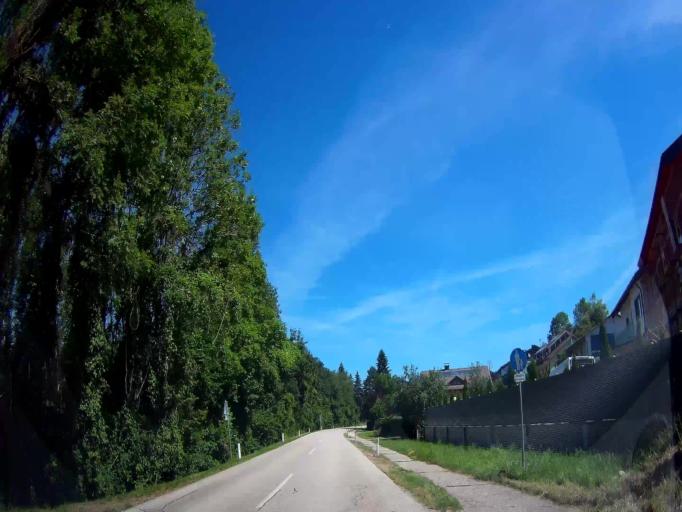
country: AT
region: Carinthia
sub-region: Politischer Bezirk Sankt Veit an der Glan
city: St. Georgen am Laengsee
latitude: 46.7732
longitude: 14.4243
